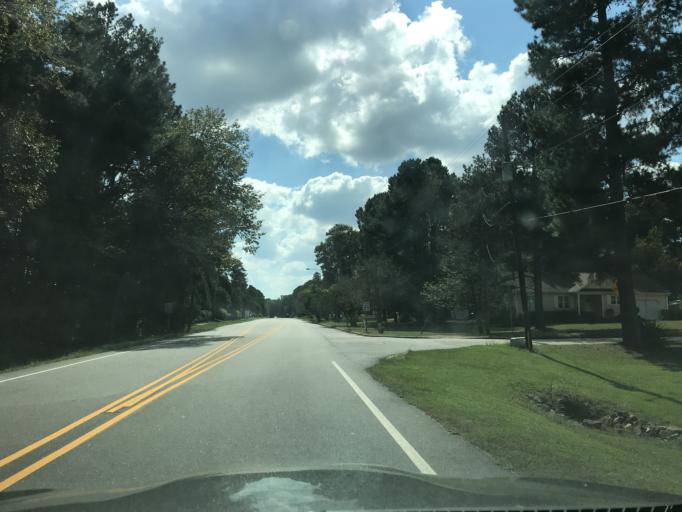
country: US
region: North Carolina
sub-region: Wake County
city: Wake Forest
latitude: 35.9443
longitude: -78.5307
